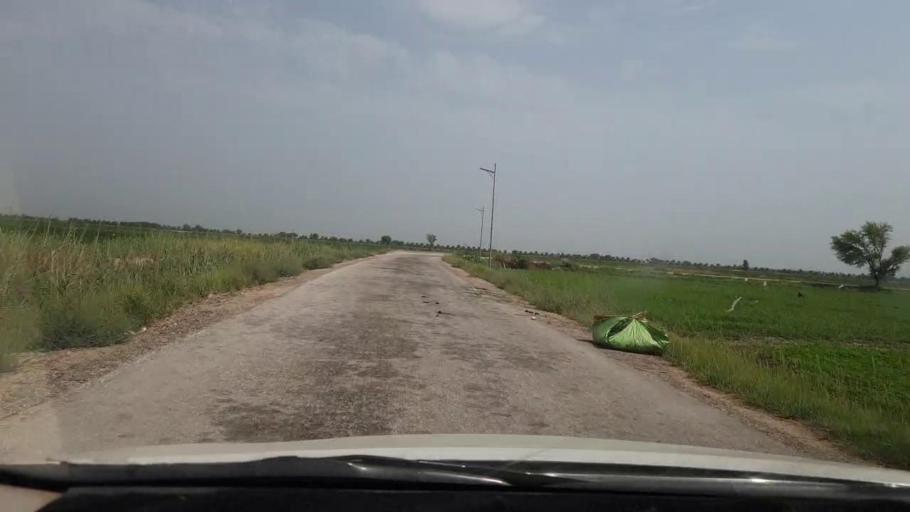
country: PK
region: Sindh
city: Rohri
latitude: 27.5377
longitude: 69.0042
